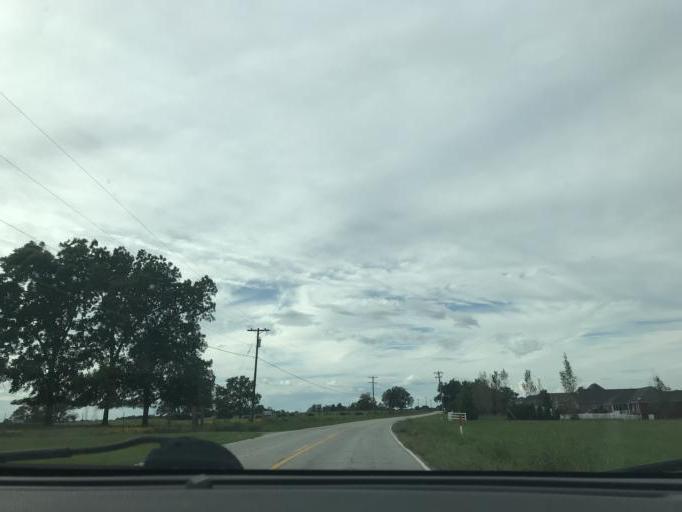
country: US
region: South Carolina
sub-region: Cherokee County
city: East Gaffney
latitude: 35.1271
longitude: -81.6631
